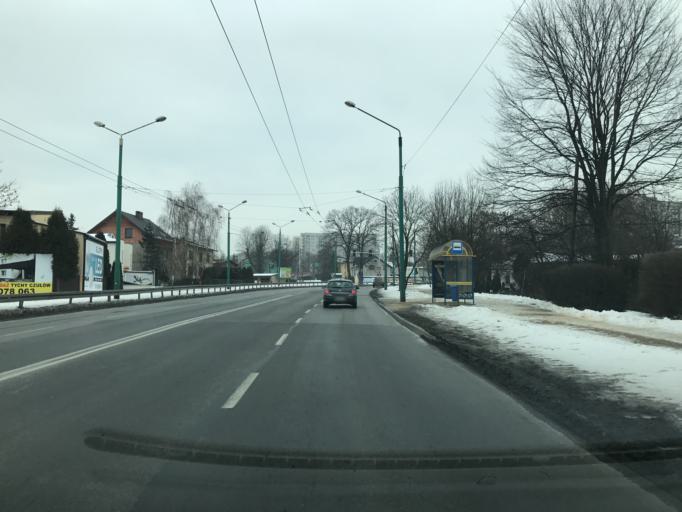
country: PL
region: Silesian Voivodeship
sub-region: Tychy
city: Cielmice
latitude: 50.1012
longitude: 18.9988
